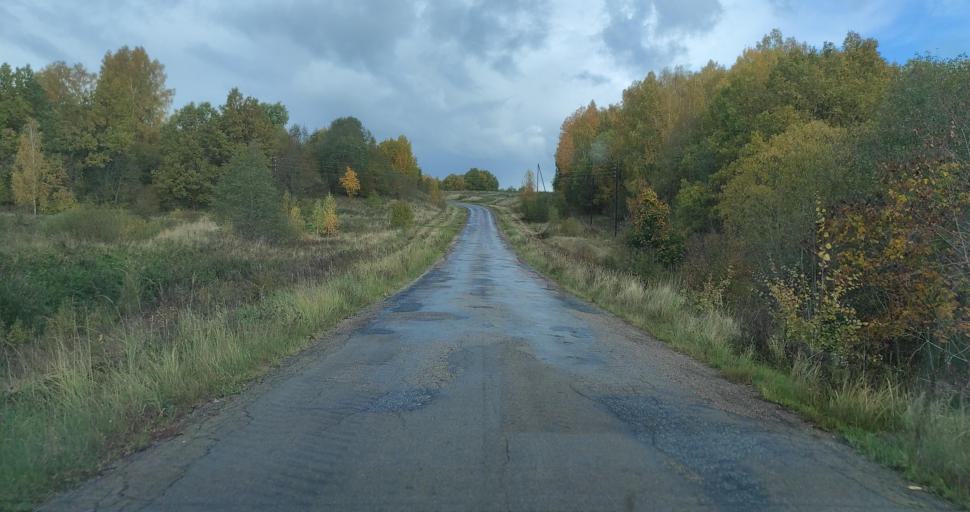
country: LV
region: Vainode
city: Vainode
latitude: 56.5636
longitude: 21.9069
